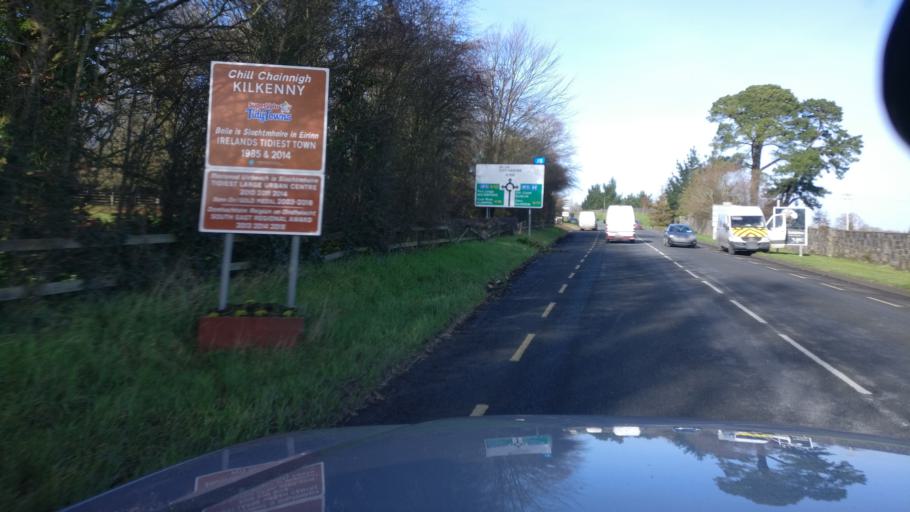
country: IE
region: Leinster
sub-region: Kilkenny
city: Kilkenny
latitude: 52.6392
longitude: -7.2284
